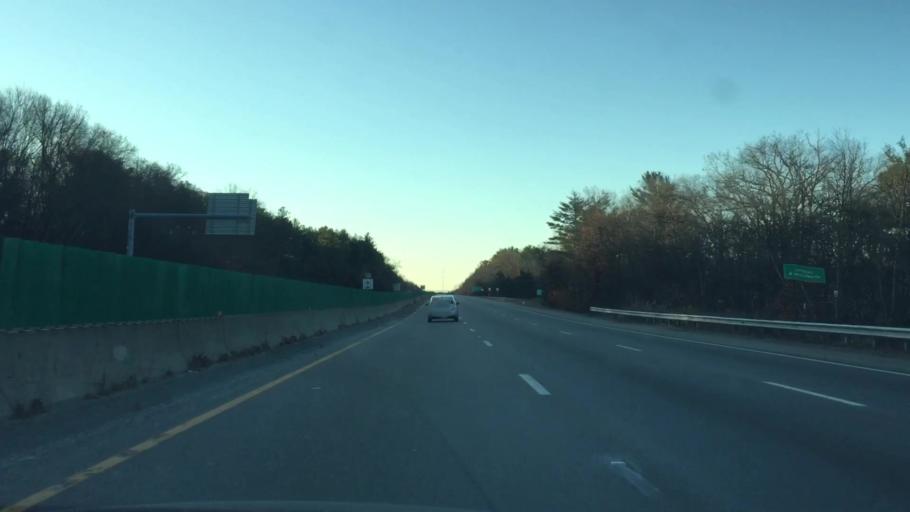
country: US
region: Massachusetts
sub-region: Plymouth County
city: Brockton
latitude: 42.0513
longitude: -71.0583
